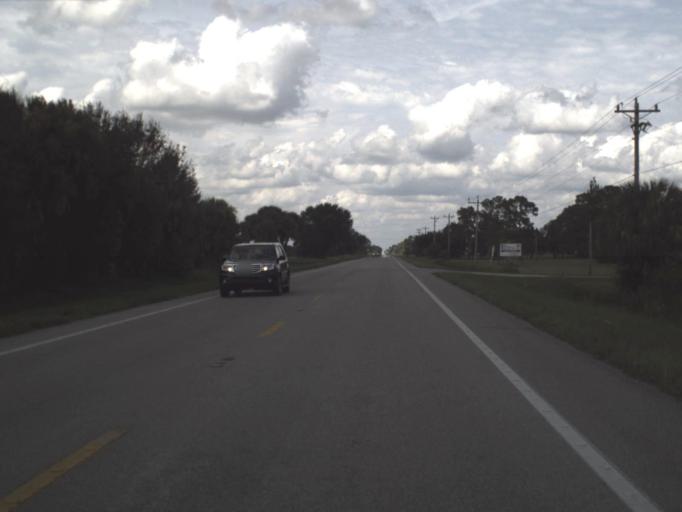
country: US
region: Florida
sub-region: Collier County
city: Immokalee
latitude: 26.5255
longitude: -81.4352
